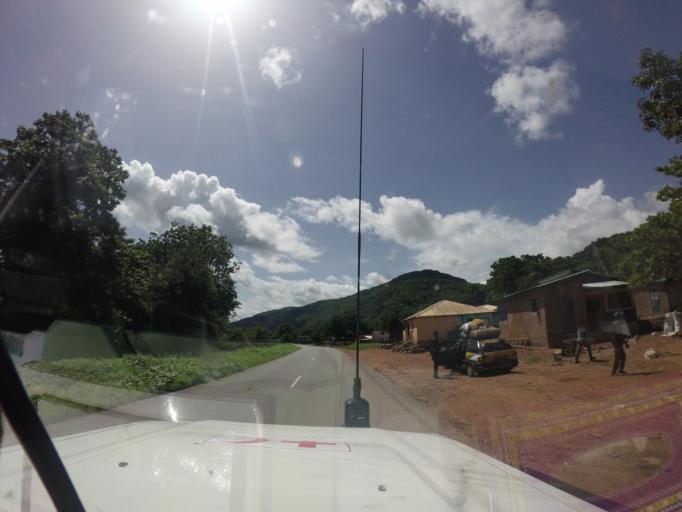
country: GN
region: Mamou
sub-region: Mamou Prefecture
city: Mamou
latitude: 10.2174
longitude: -11.8556
